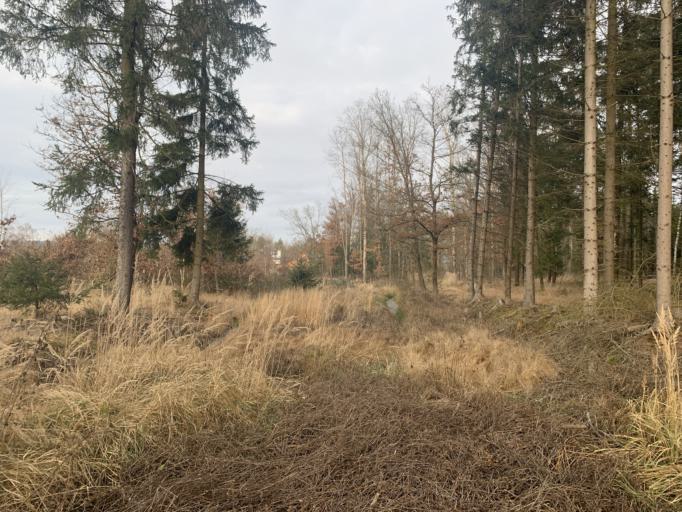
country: CZ
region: Plzensky
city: Zbiroh
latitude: 49.8285
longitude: 13.7964
